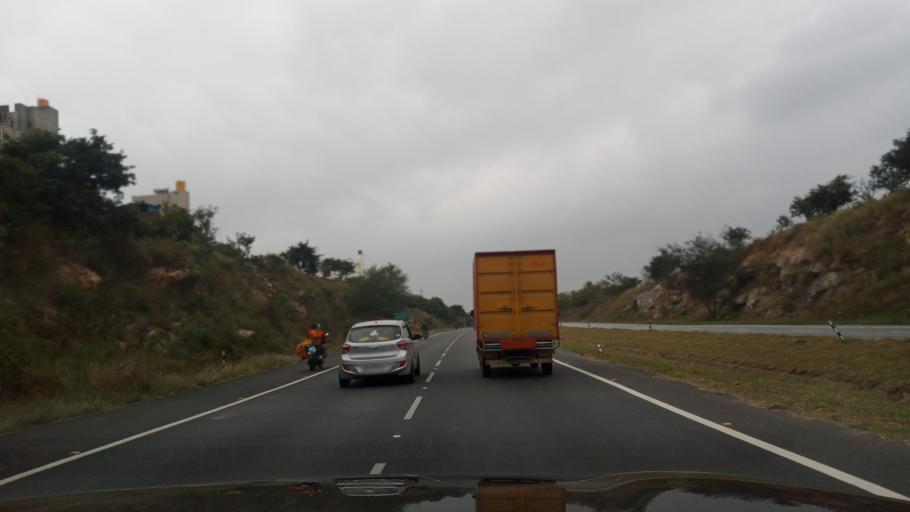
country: IN
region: Karnataka
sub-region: Bangalore Rural
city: Nelamangala
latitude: 13.0126
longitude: 77.4758
